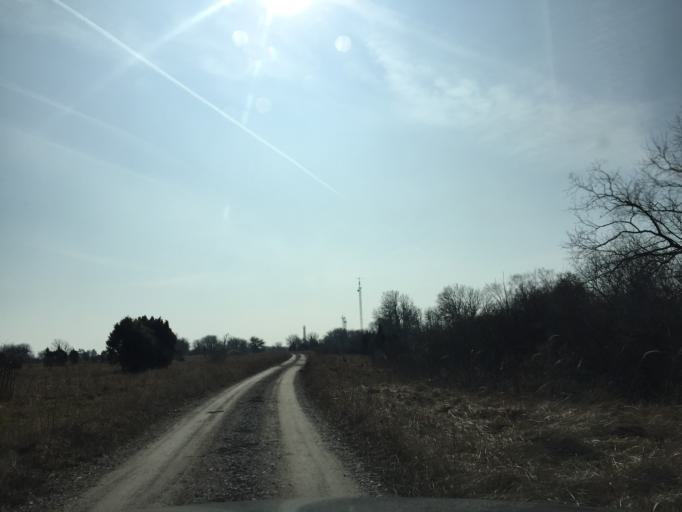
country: LV
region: Dundaga
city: Dundaga
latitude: 57.9211
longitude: 22.0605
